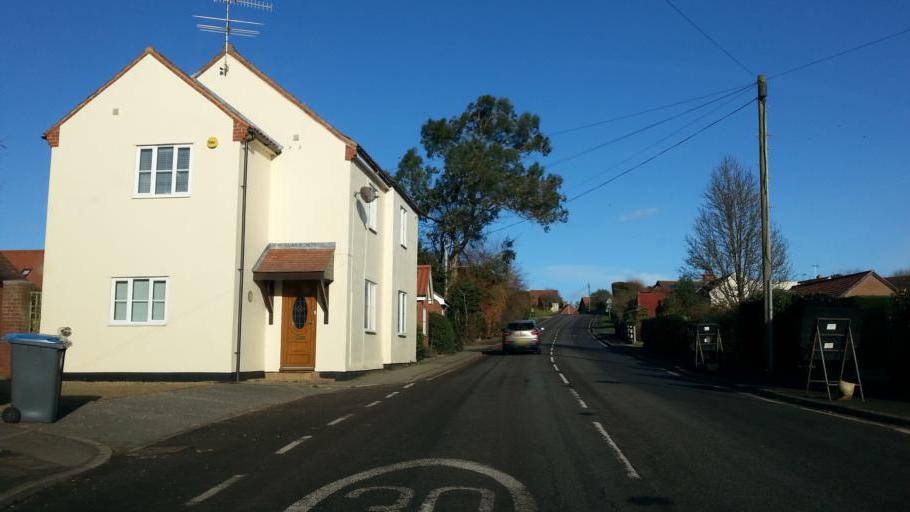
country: GB
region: England
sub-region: Suffolk
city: Saxmundham
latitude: 52.1692
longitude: 1.4998
